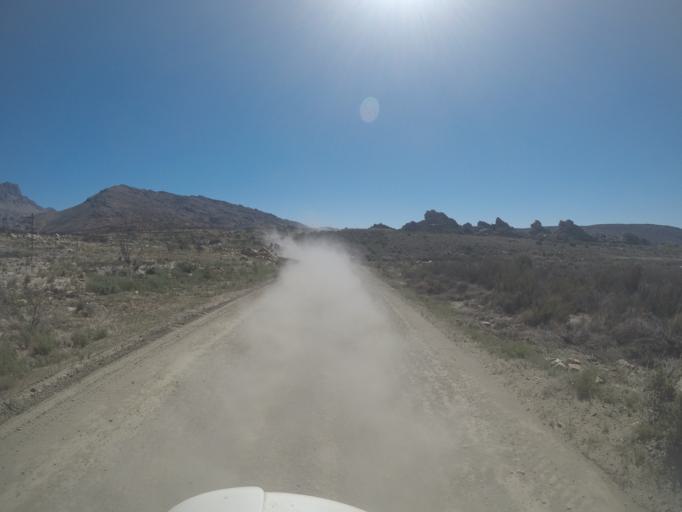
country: ZA
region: Western Cape
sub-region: Cape Winelands District Municipality
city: Ceres
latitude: -32.8579
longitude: 19.4441
